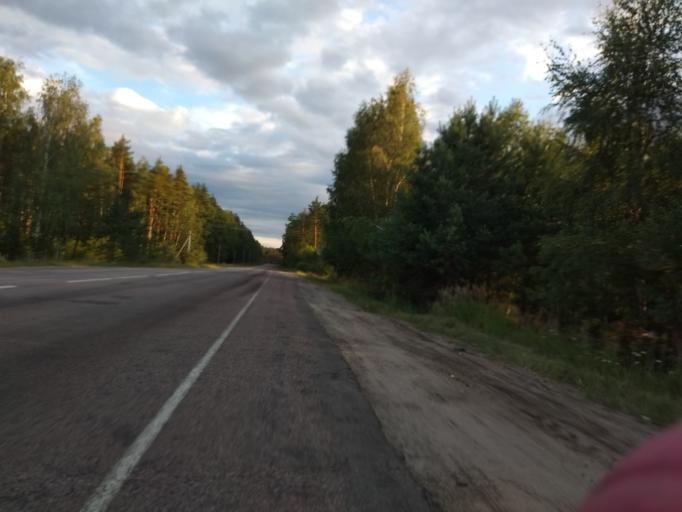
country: RU
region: Moskovskaya
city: Misheronskiy
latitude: 55.6329
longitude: 39.7451
